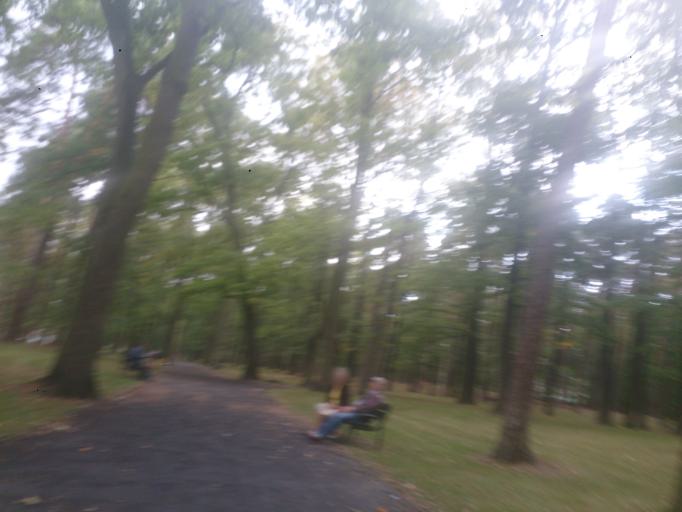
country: PL
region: Kujawsko-Pomorskie
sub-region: Grudziadz
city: Grudziadz
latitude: 53.4763
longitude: 18.7586
